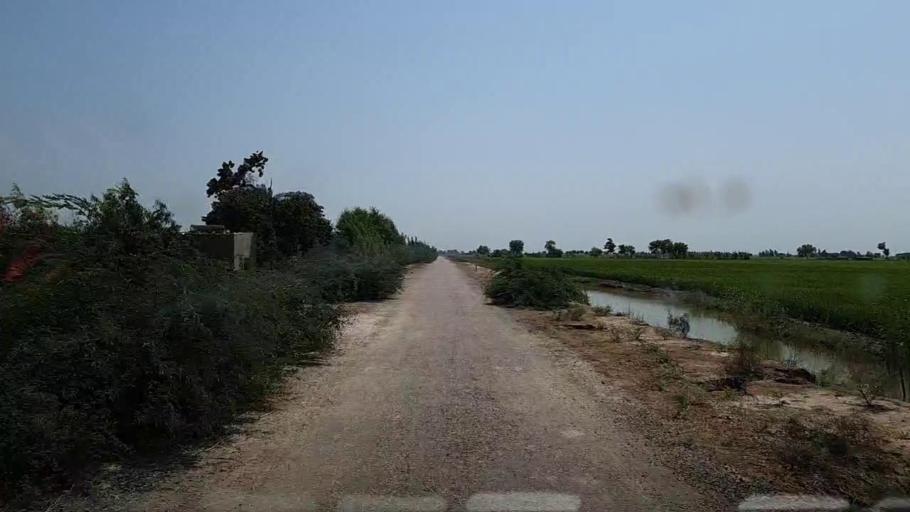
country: PK
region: Sindh
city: Mirpur Batoro
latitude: 24.6132
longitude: 68.4523
